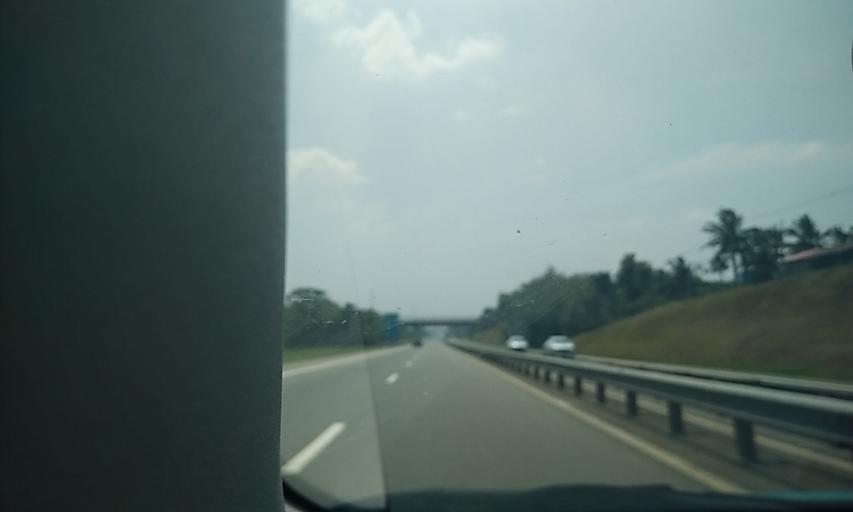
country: LK
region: Western
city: Horana South
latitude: 6.7310
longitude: 79.9989
